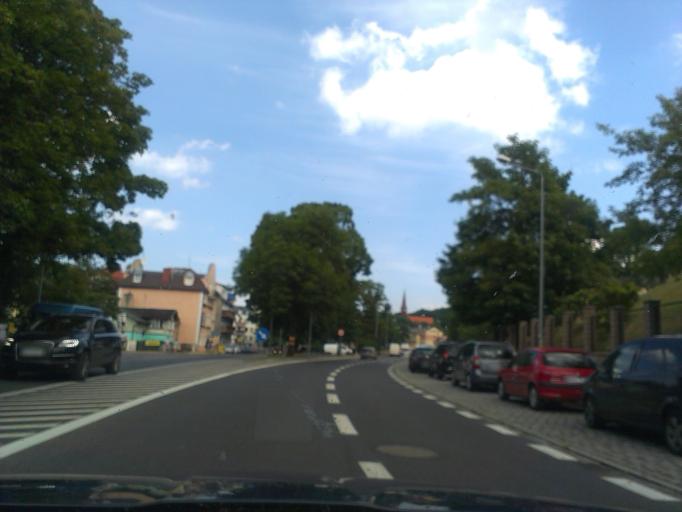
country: PL
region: West Pomeranian Voivodeship
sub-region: Powiat kamienski
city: Miedzyzdroje
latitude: 53.9269
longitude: 14.4493
